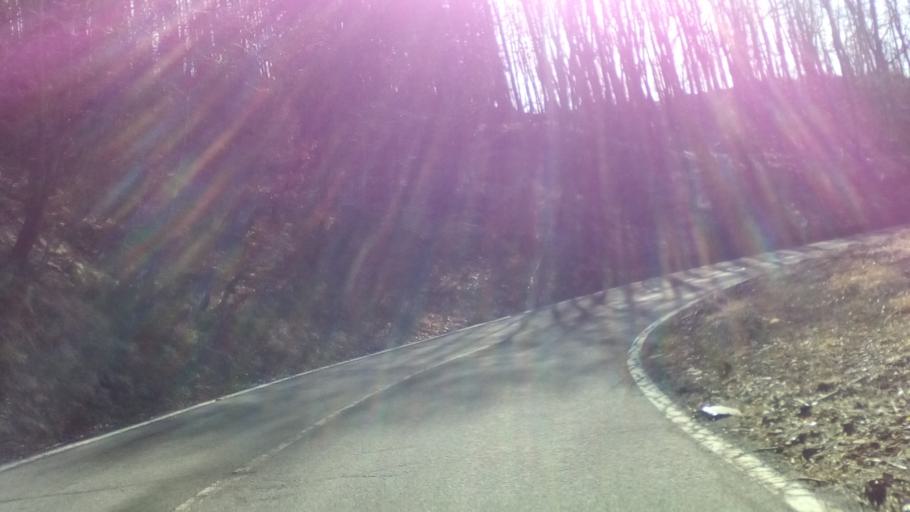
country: IT
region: Emilia-Romagna
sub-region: Provincia di Modena
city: Pievepelago
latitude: 44.2179
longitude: 10.6170
